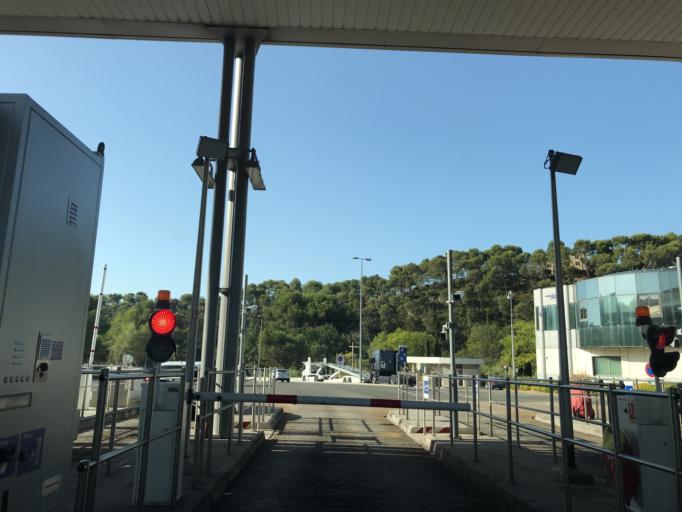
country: FR
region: Provence-Alpes-Cote d'Azur
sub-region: Departement du Var
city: Bandol
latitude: 43.1445
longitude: 5.7685
